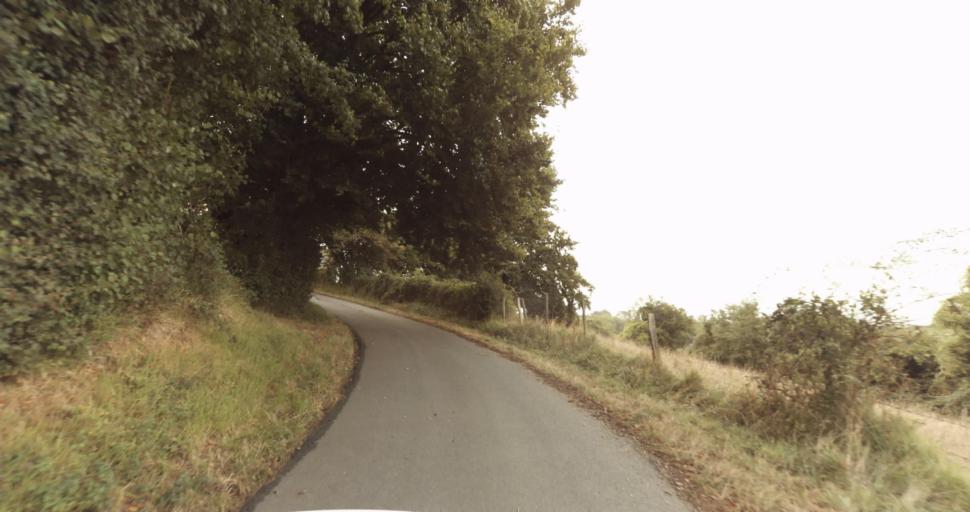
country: FR
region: Lower Normandy
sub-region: Departement de l'Orne
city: Trun
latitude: 48.8988
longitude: 0.1034
